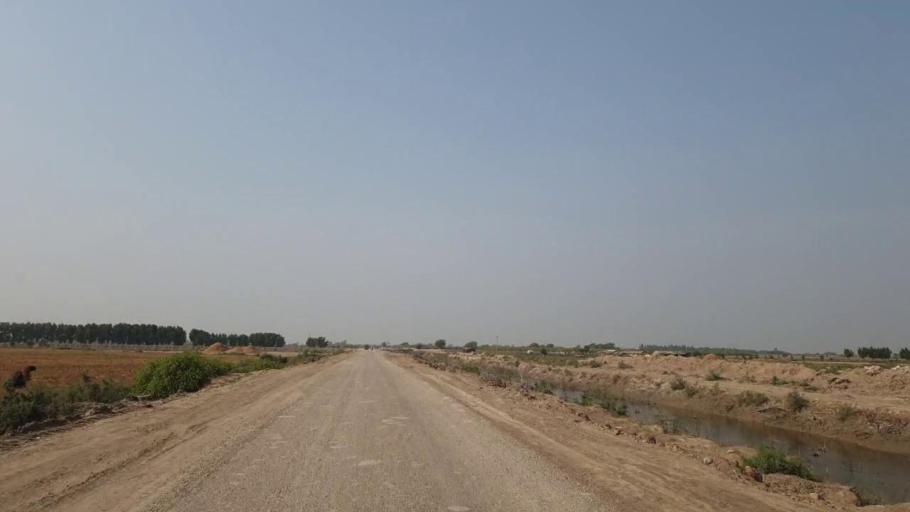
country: PK
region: Sindh
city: Tando Muhammad Khan
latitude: 24.9713
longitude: 68.5084
